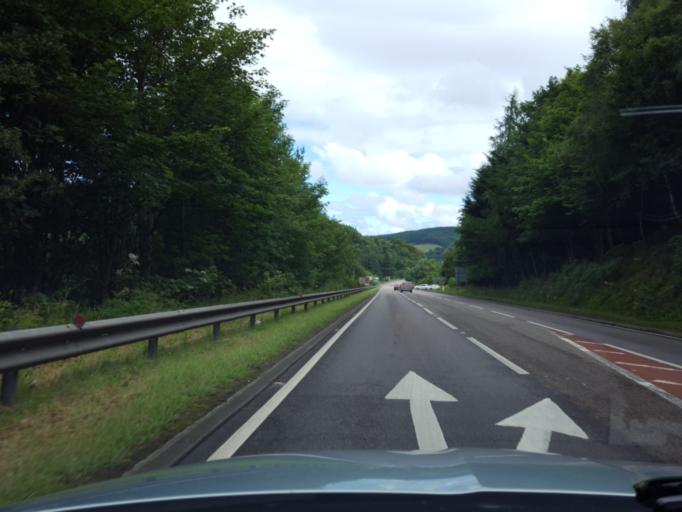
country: GB
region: Scotland
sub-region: Moray
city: Rothes
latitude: 57.4856
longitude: -3.1939
